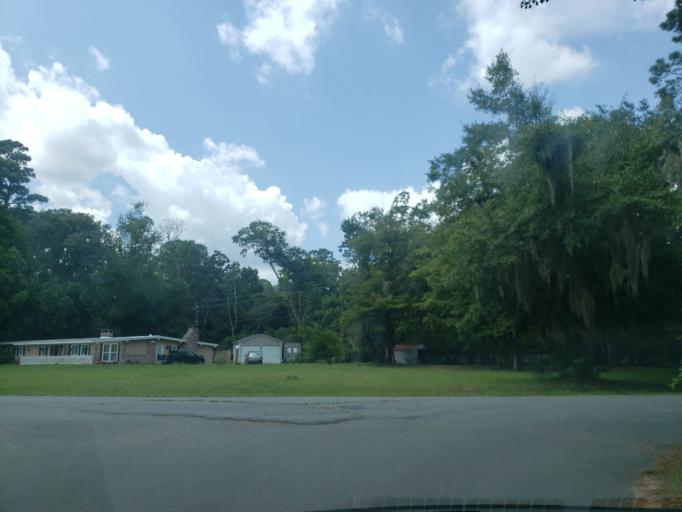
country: US
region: Georgia
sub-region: Chatham County
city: Isle of Hope
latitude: 31.9878
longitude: -81.0505
